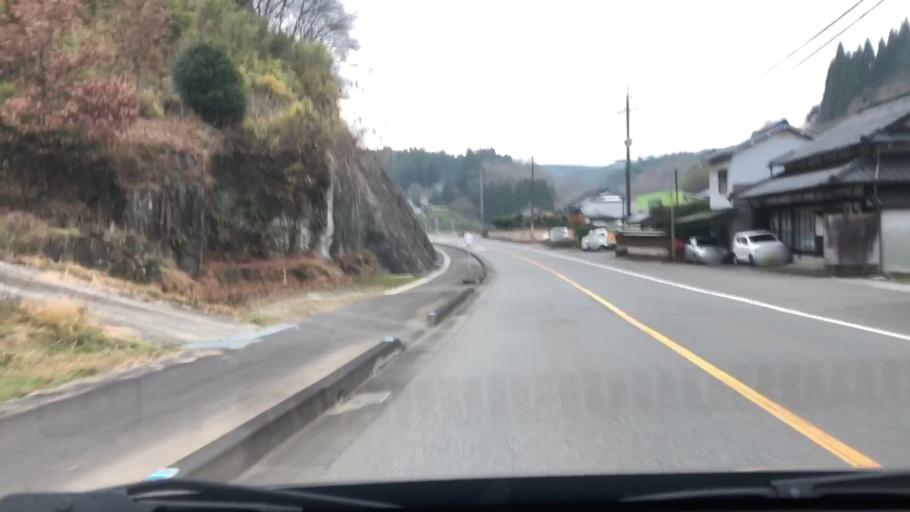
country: JP
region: Oita
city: Usuki
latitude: 33.0076
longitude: 131.6468
